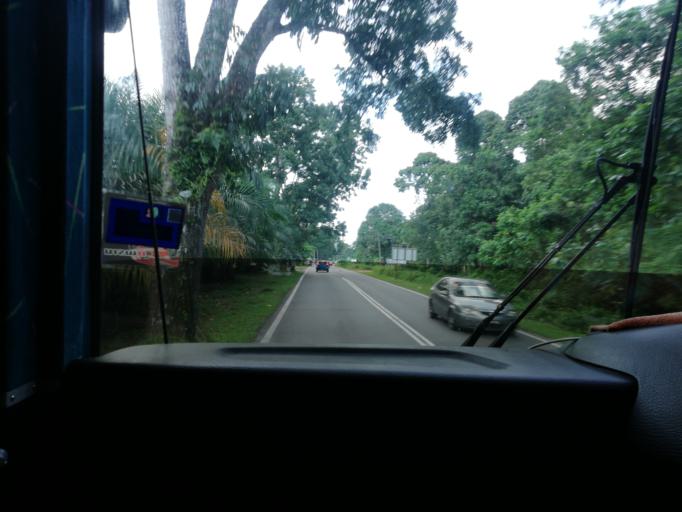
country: MY
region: Kedah
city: Kulim
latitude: 5.3540
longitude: 100.5833
